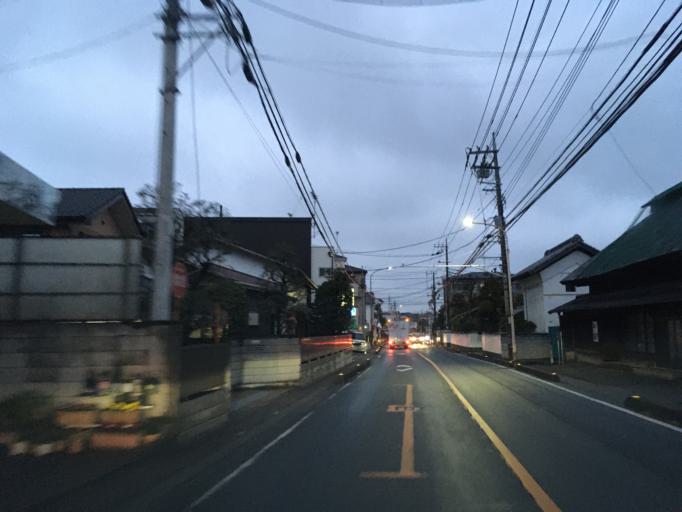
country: JP
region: Saitama
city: Asaka
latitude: 35.7924
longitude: 139.5831
